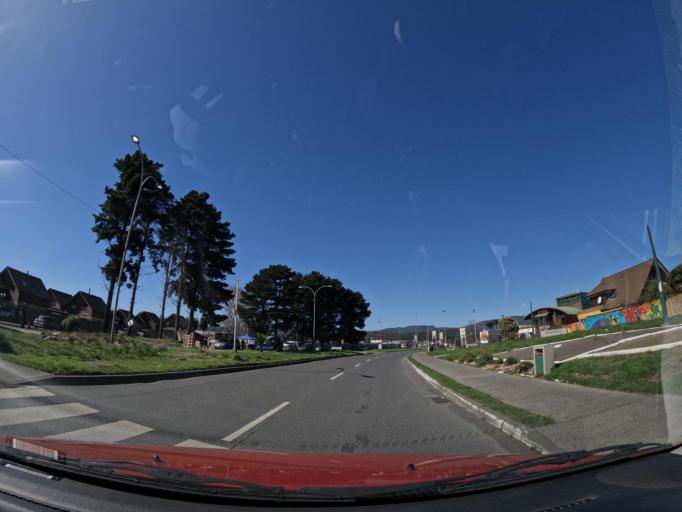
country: CL
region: Biobio
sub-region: Provincia de Concepcion
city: Concepcion
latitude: -36.8826
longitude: -73.1420
